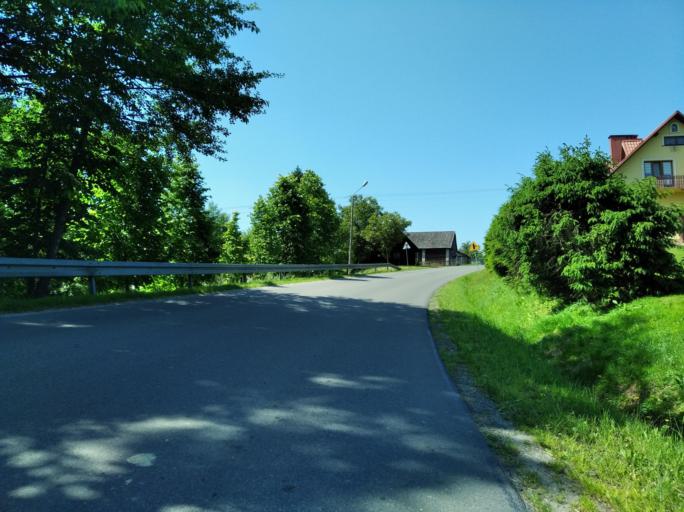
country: PL
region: Subcarpathian Voivodeship
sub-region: Powiat ropczycko-sedziszowski
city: Zagorzyce
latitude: 50.0047
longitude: 21.6579
